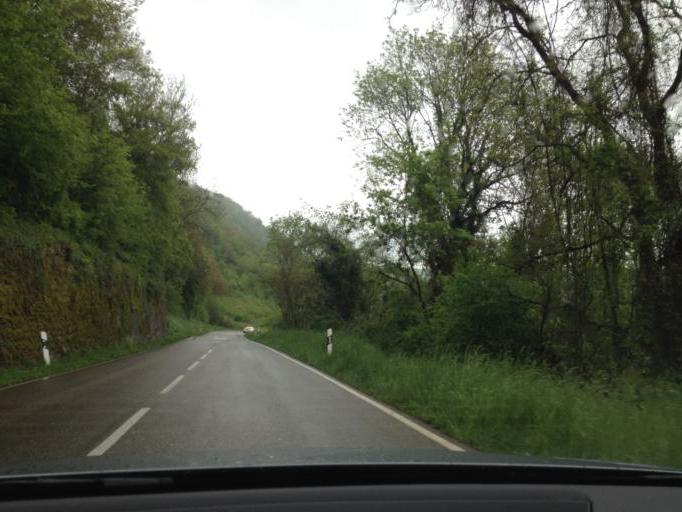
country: DE
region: Baden-Wuerttemberg
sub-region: Regierungsbezirk Stuttgart
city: Gundelsheim
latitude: 49.2667
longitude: 9.1475
